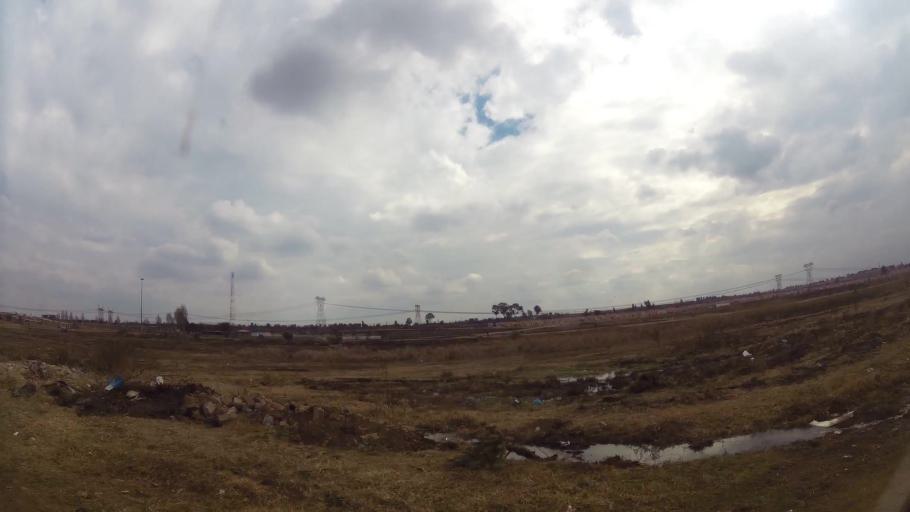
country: ZA
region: Gauteng
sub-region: Ekurhuleni Metropolitan Municipality
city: Germiston
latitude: -26.3771
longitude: 28.1163
